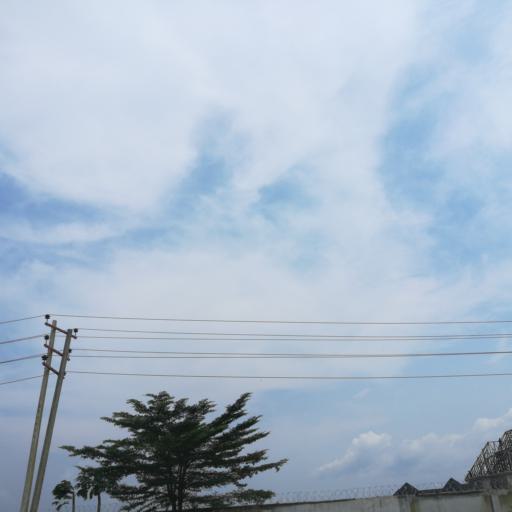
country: NG
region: Rivers
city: Port Harcourt
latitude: 4.8479
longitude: 7.0150
